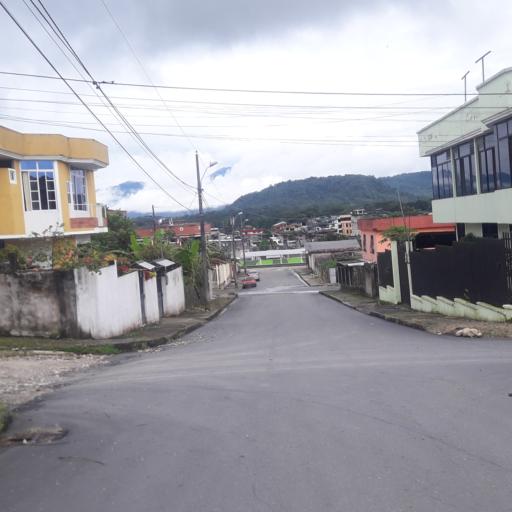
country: EC
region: Napo
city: Tena
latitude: -0.9983
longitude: -77.8084
